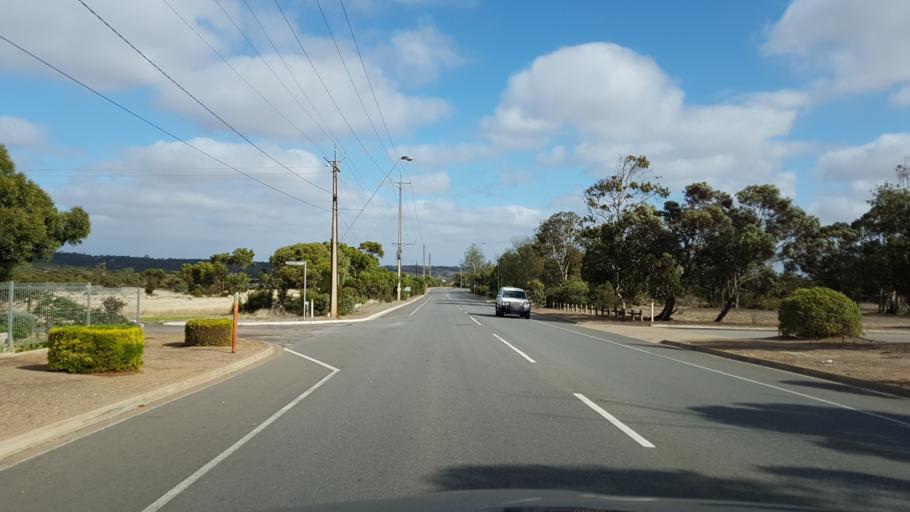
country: AU
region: South Australia
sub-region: Murray Bridge
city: Murray Bridge
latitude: -35.1188
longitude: 139.2492
